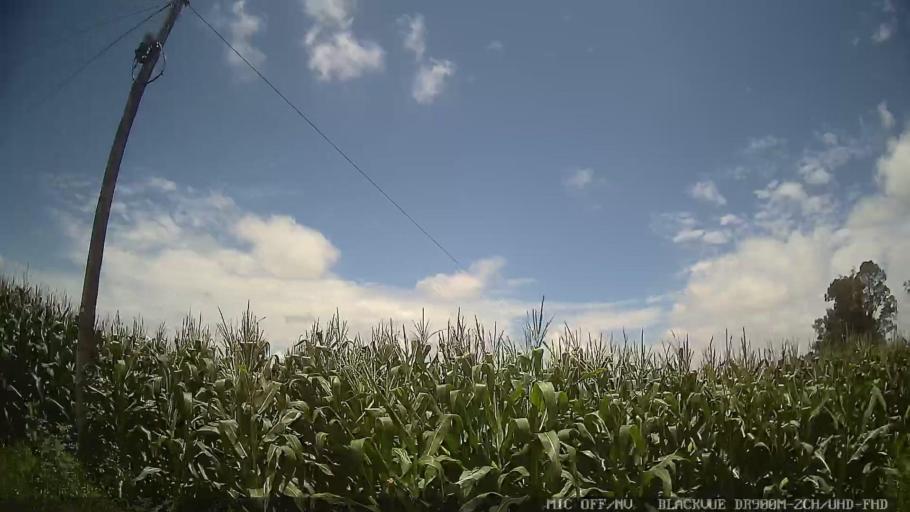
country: BR
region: Sao Paulo
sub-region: Laranjal Paulista
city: Laranjal Paulista
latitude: -23.0266
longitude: -47.8578
